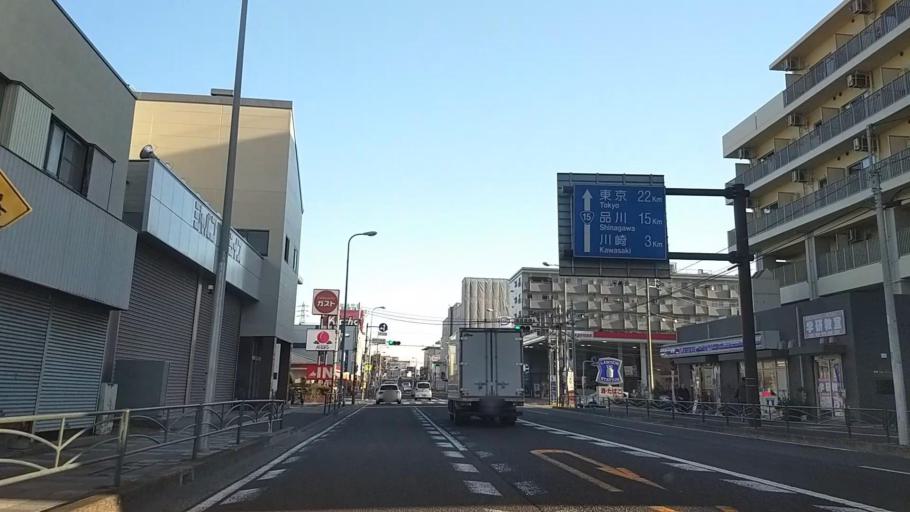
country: JP
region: Kanagawa
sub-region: Kawasaki-shi
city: Kawasaki
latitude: 35.5096
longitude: 139.6826
